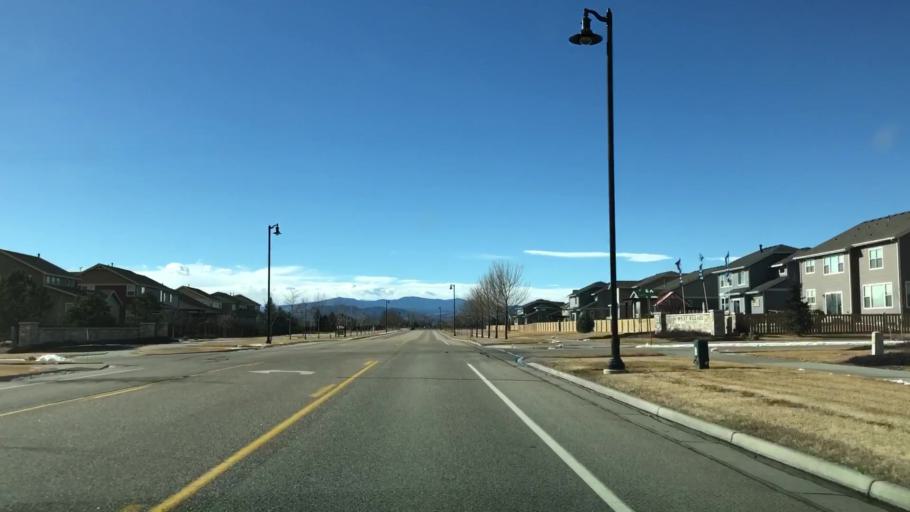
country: US
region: Colorado
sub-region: Weld County
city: Windsor
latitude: 40.5089
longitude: -104.9605
